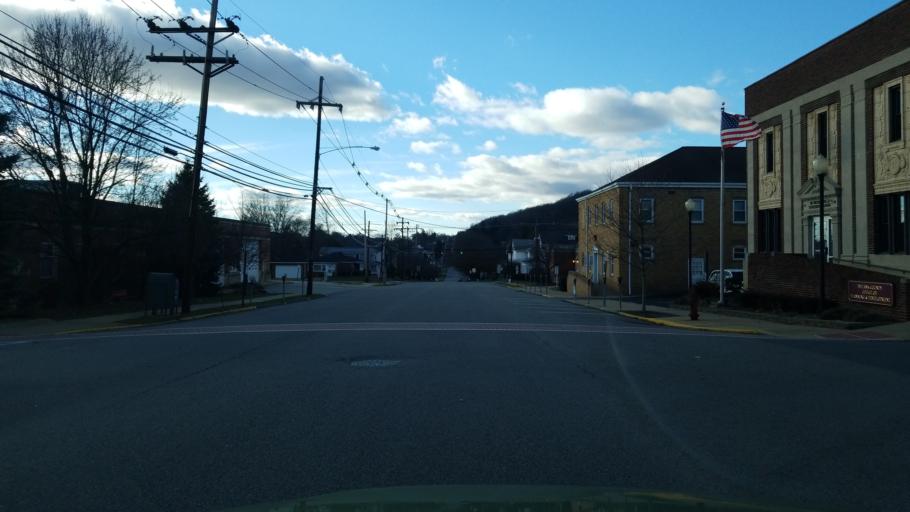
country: US
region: Pennsylvania
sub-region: Indiana County
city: Indiana
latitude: 40.6244
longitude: -79.1545
